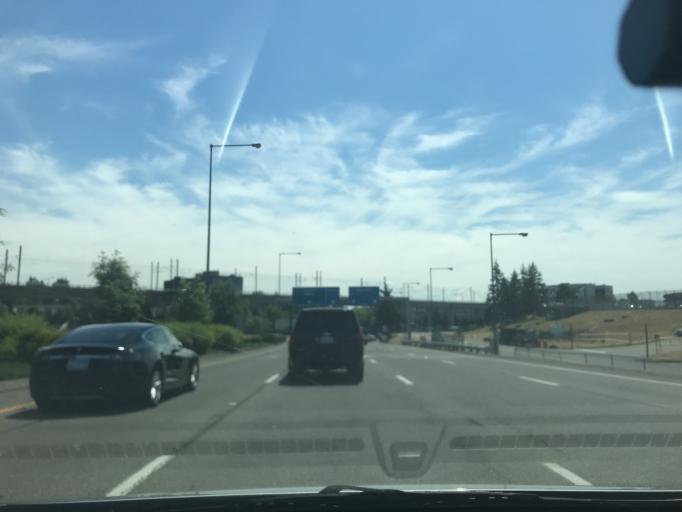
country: US
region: Washington
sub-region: King County
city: SeaTac
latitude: 47.4489
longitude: -122.2994
